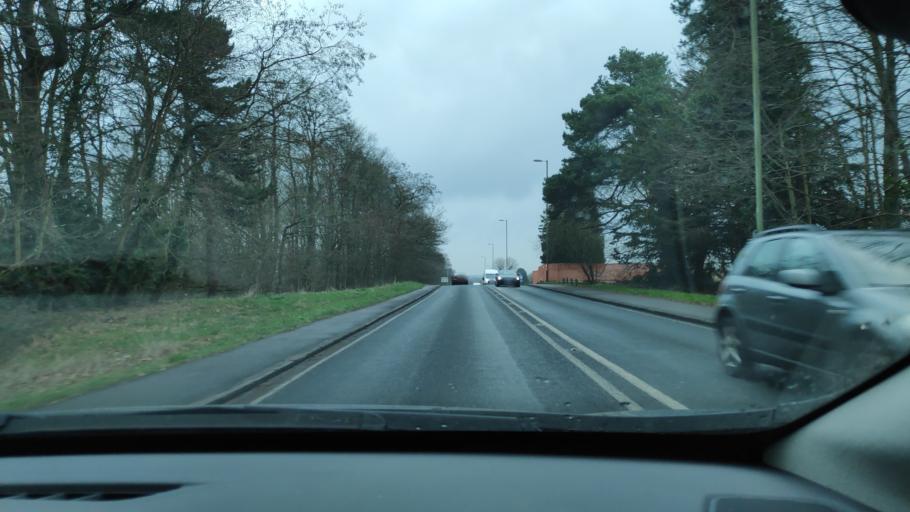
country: GB
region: England
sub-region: Hampshire
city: Aldershot
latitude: 51.2560
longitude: -0.7724
